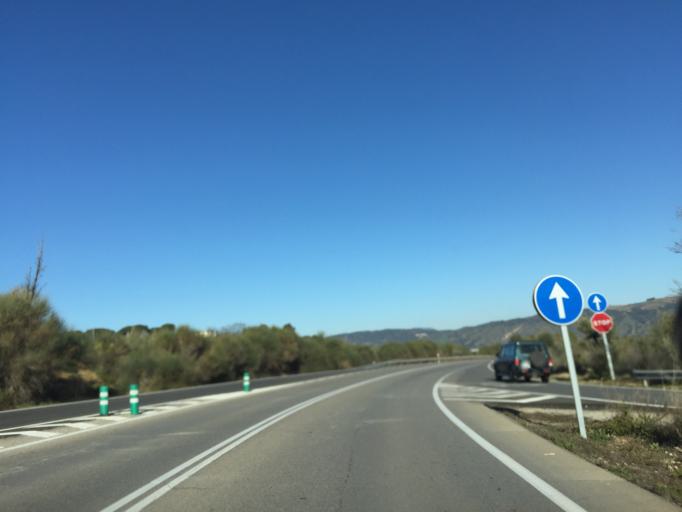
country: ES
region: Andalusia
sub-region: Provincia de Malaga
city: Ronda
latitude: 36.7554
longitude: -5.1540
